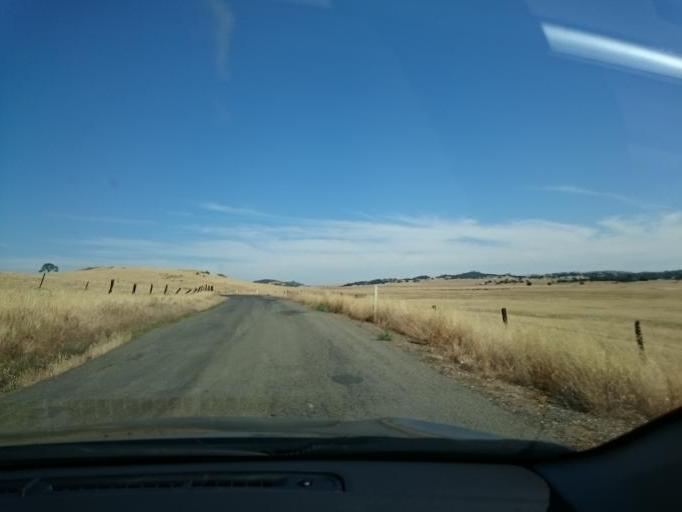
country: US
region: California
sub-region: Calaveras County
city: Copperopolis
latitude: 38.0504
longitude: -120.7222
